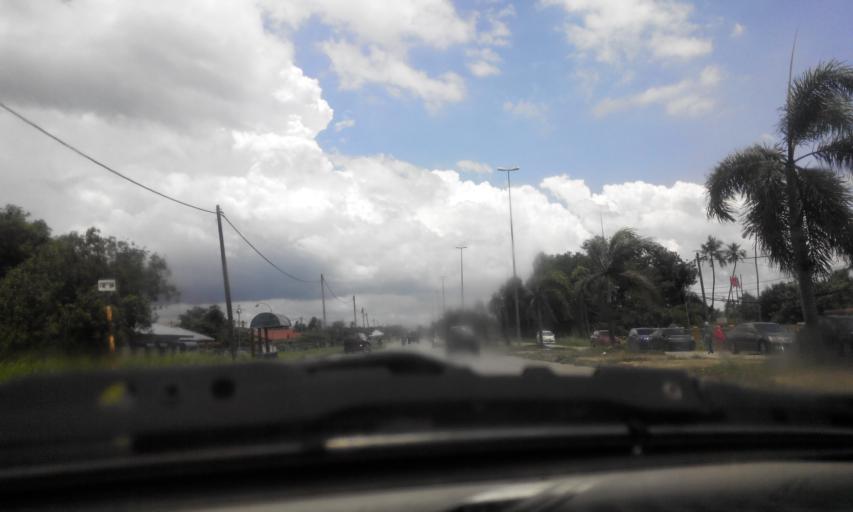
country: MY
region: Perak
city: Parit Buntar
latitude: 5.1174
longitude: 100.5248
